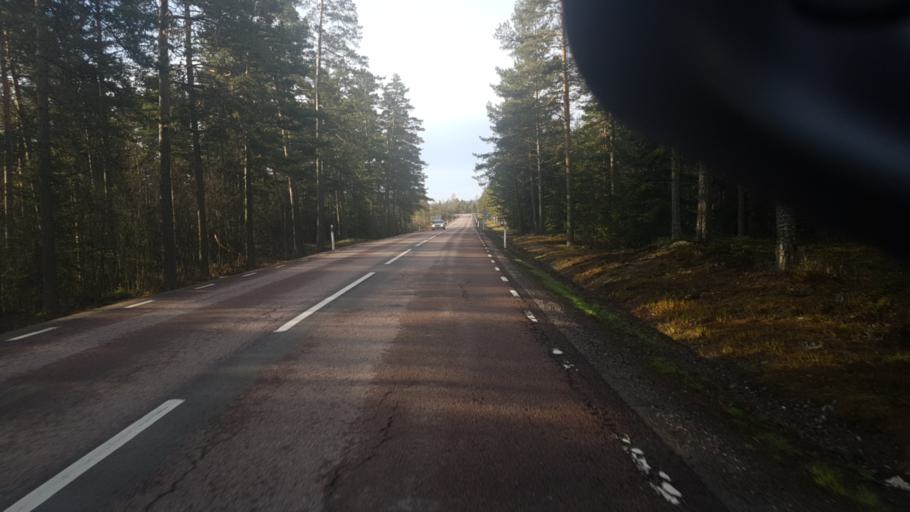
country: SE
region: Vaermland
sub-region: Eda Kommun
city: Charlottenberg
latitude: 59.8543
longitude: 12.3080
